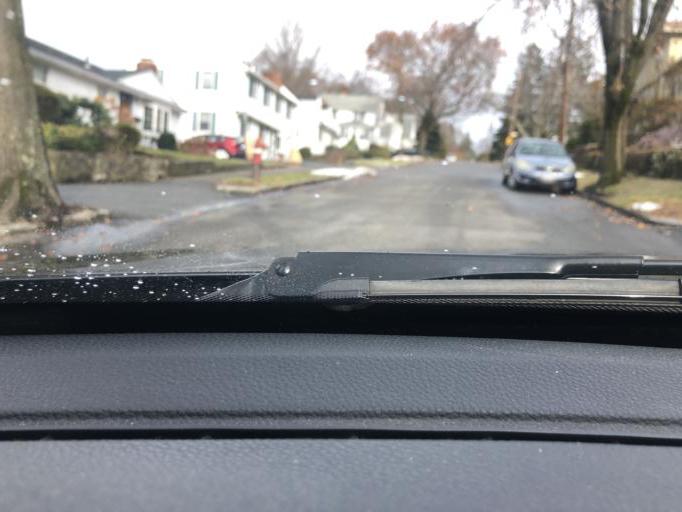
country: US
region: Massachusetts
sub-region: Middlesex County
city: Arlington
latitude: 42.4253
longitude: -71.1643
